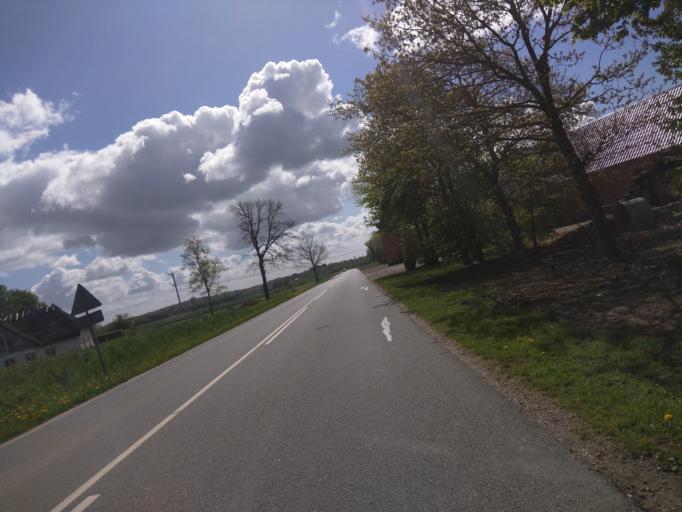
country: DK
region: Central Jutland
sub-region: Silkeborg Kommune
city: Kjellerup
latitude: 56.2815
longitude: 9.4810
